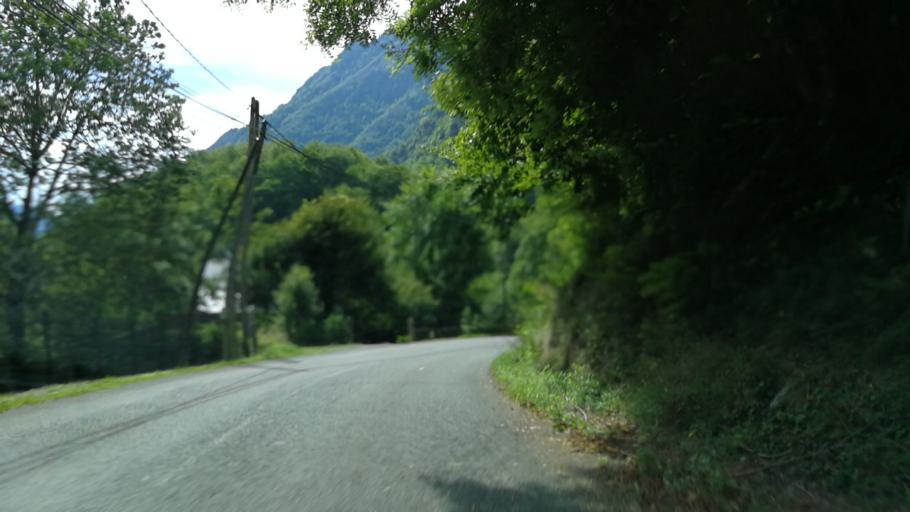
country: FR
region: Aquitaine
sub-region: Departement des Pyrenees-Atlantiques
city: Arette
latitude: 42.9457
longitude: -0.6113
